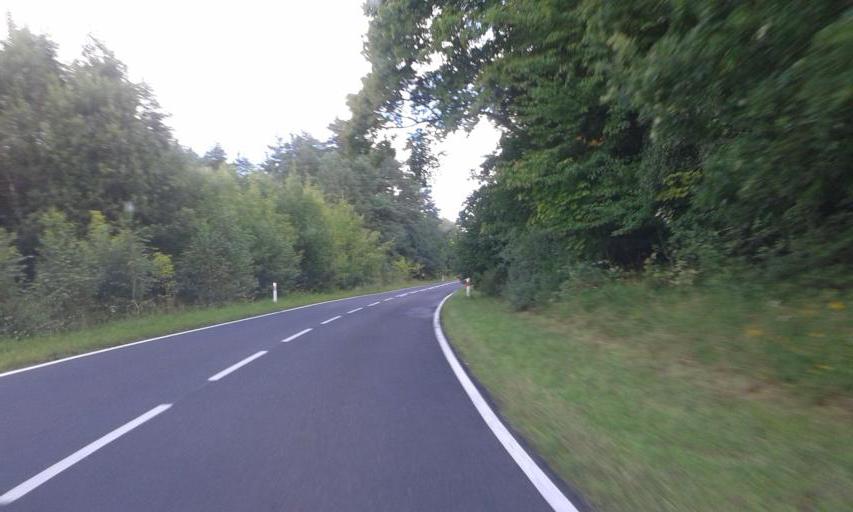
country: PL
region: West Pomeranian Voivodeship
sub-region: Powiat koszalinski
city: Polanow
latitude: 54.0125
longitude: 16.7191
